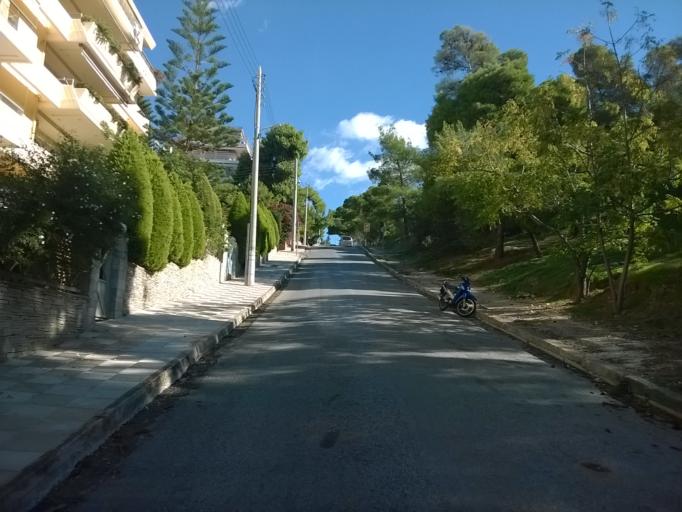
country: GR
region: Attica
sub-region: Nomarchia Anatolikis Attikis
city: Vouliagmeni
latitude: 37.8142
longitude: 23.7869
